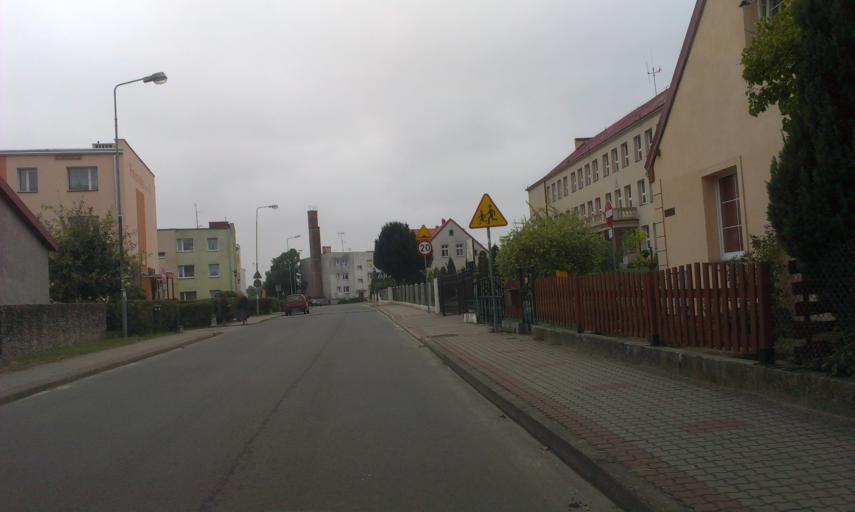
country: PL
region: West Pomeranian Voivodeship
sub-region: Powiat szczecinecki
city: Barwice
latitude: 53.7468
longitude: 16.3536
